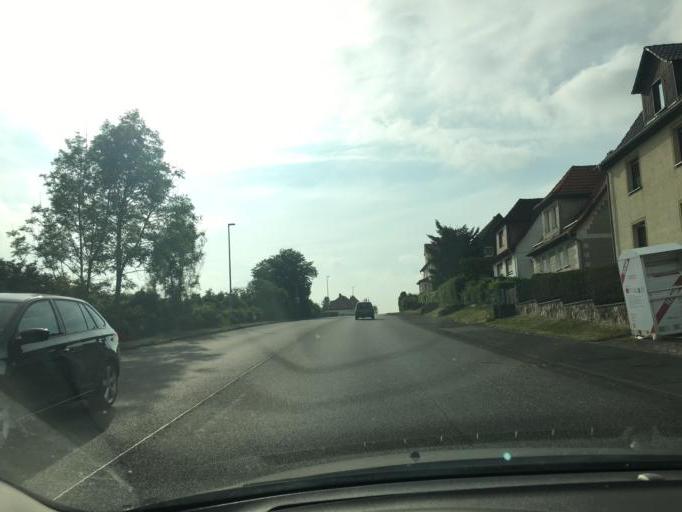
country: DE
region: Hesse
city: Hessisch Lichtenau
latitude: 51.1982
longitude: 9.7748
